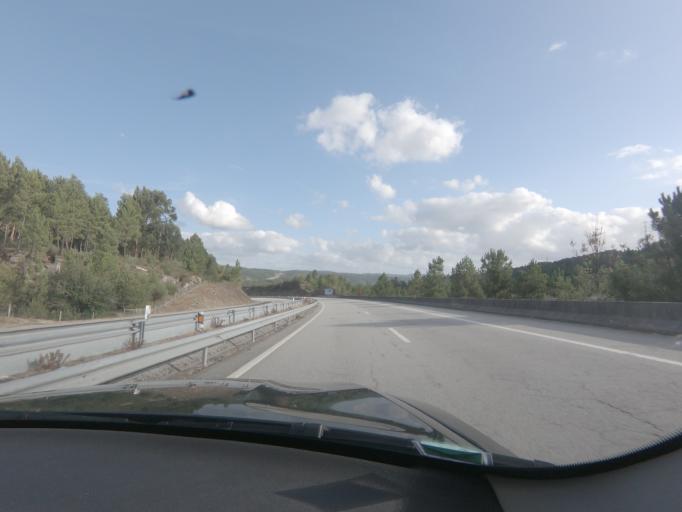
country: PT
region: Viseu
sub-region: Castro Daire
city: Castro Daire
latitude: 40.8114
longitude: -7.9388
